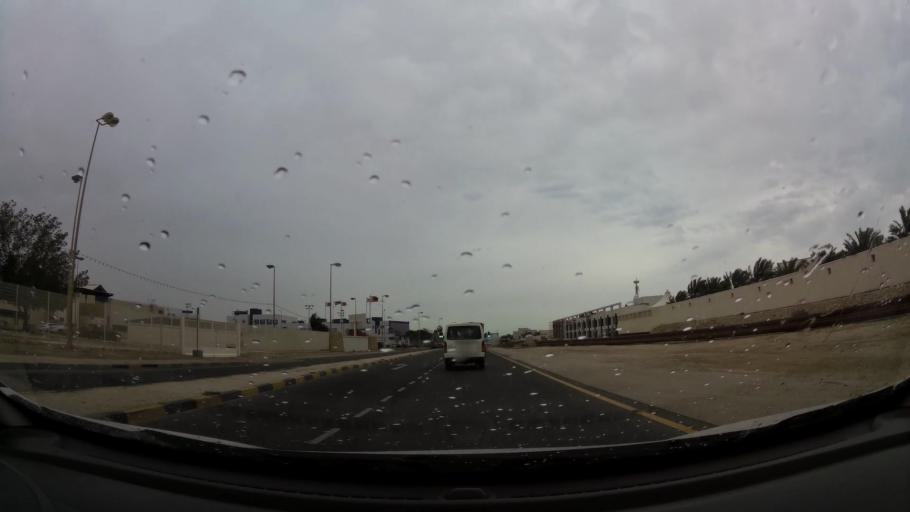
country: BH
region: Central Governorate
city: Madinat Hamad
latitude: 26.1619
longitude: 50.4736
